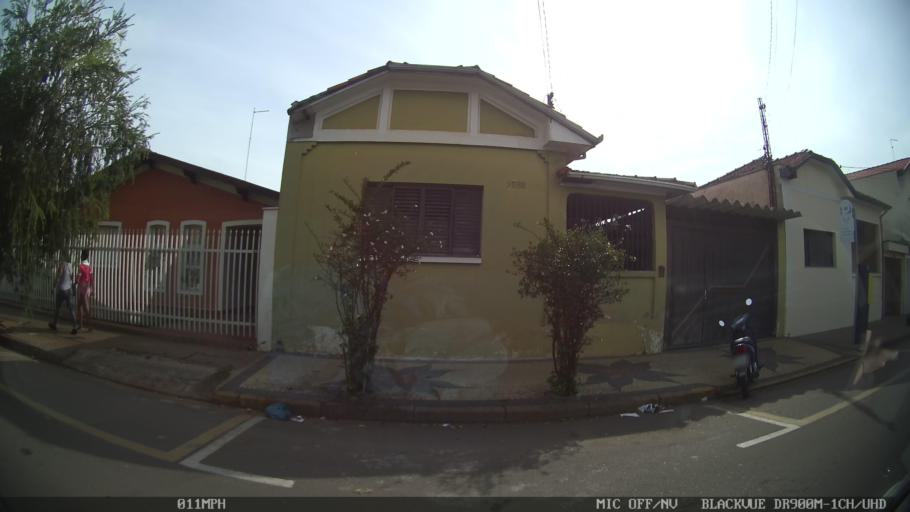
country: BR
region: Sao Paulo
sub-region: Piracicaba
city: Piracicaba
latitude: -22.7378
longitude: -47.6578
